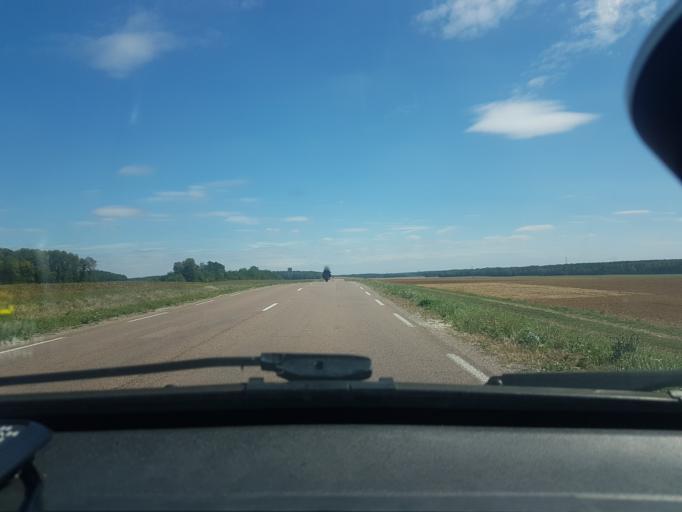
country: FR
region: Bourgogne
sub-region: Departement de la Cote-d'Or
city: Pontailler-sur-Saone
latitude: 47.3997
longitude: 5.4208
